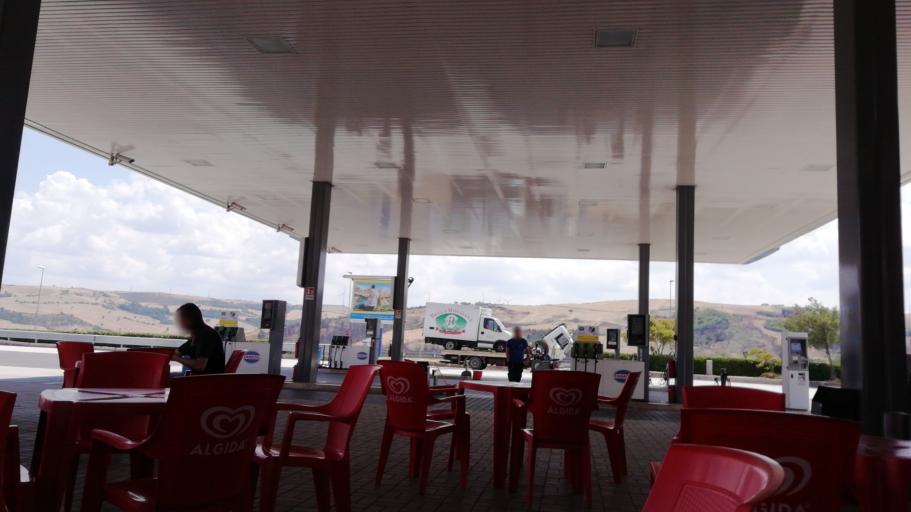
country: IT
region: Campania
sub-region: Provincia di Avellino
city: Scampitella
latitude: 41.0666
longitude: 15.3155
